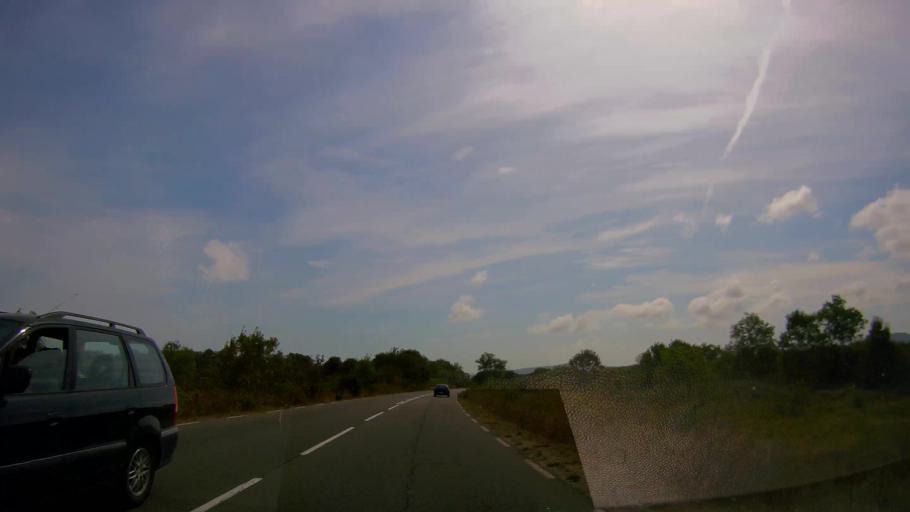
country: BG
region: Burgas
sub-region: Obshtina Sozopol
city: Sozopol
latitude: 42.3632
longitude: 27.6982
